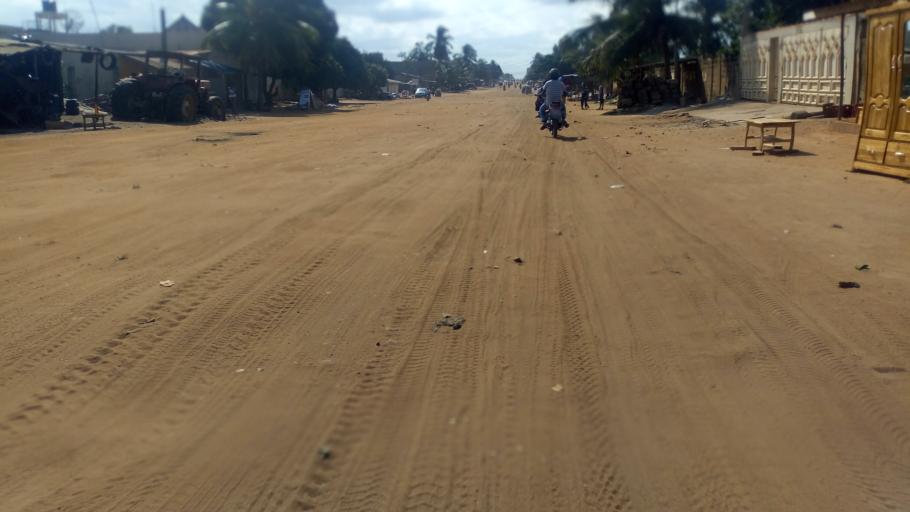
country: TG
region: Maritime
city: Lome
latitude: 6.2280
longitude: 1.1844
